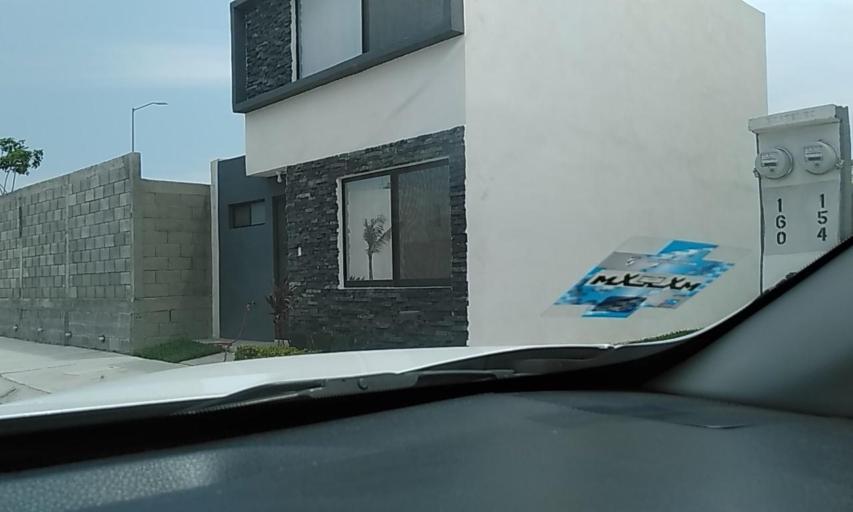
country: MX
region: Veracruz
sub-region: Veracruz
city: Las Amapolas
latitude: 19.1496
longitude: -96.2153
